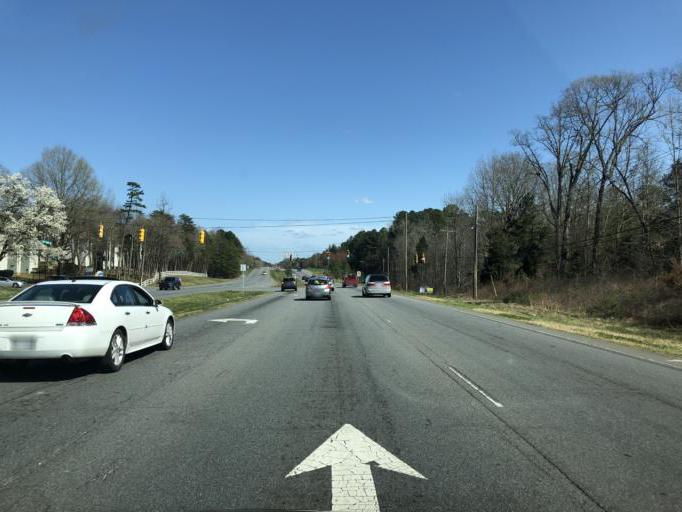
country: US
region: North Carolina
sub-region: Mecklenburg County
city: Huntersville
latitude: 35.3324
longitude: -80.8111
